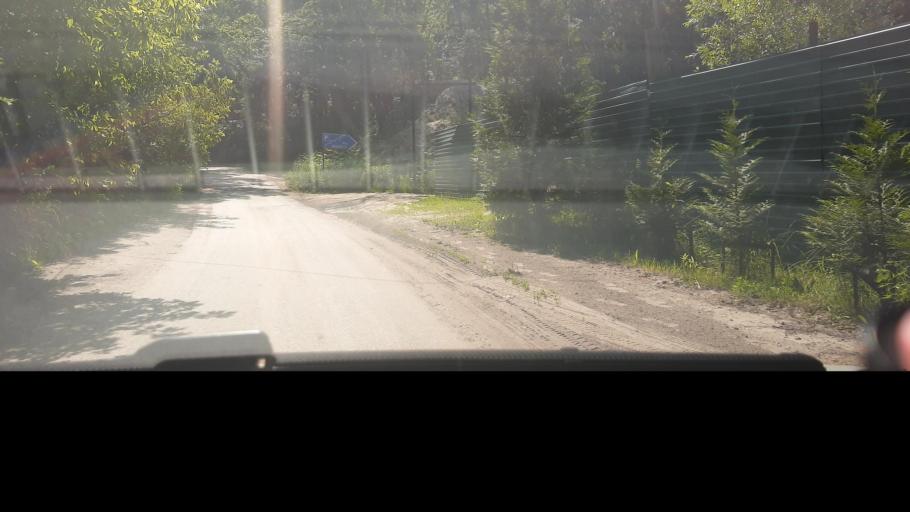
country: RU
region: Nizjnij Novgorod
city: Afonino
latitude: 56.2683
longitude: 44.1985
